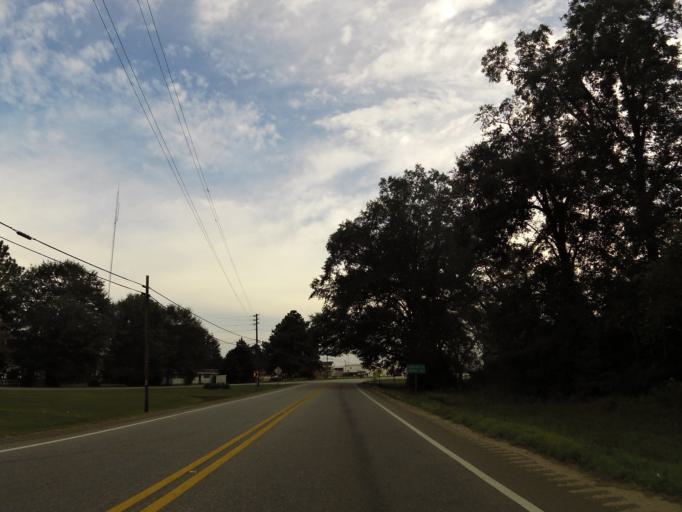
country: US
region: Alabama
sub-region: Monroe County
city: Frisco City
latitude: 31.3036
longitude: -87.5023
